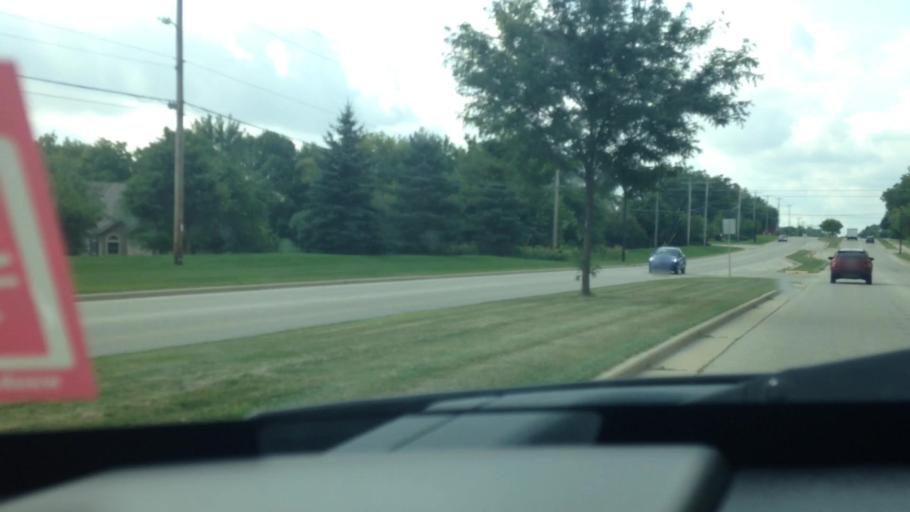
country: US
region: Wisconsin
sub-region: Waukesha County
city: Menomonee Falls
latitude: 43.1433
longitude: -88.1046
